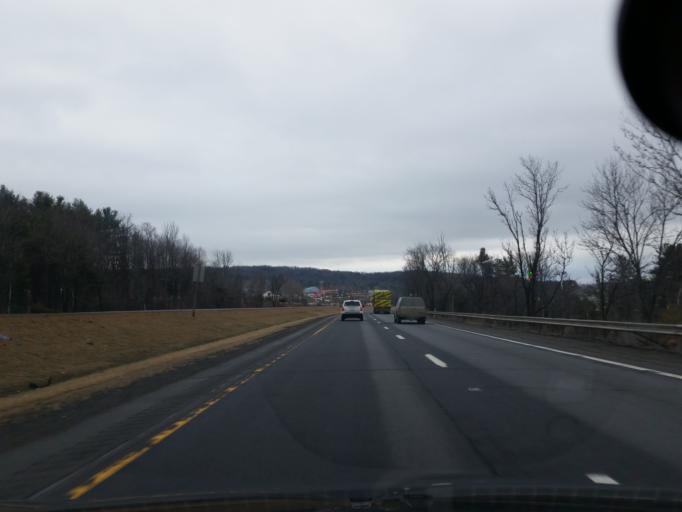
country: US
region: Pennsylvania
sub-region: Susquehanna County
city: Susquehanna
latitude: 41.8303
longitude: -75.6805
